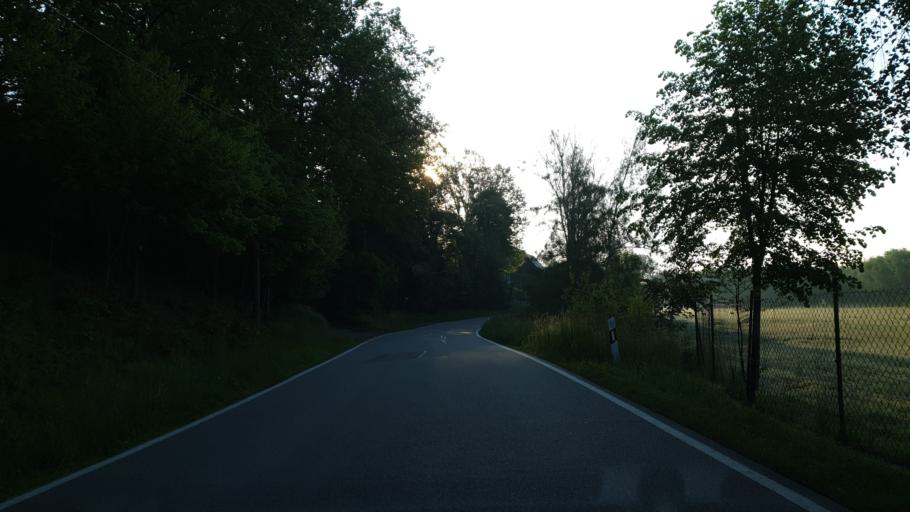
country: DE
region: Saxony
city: Sankt Egidien
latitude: 50.7854
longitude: 12.6474
